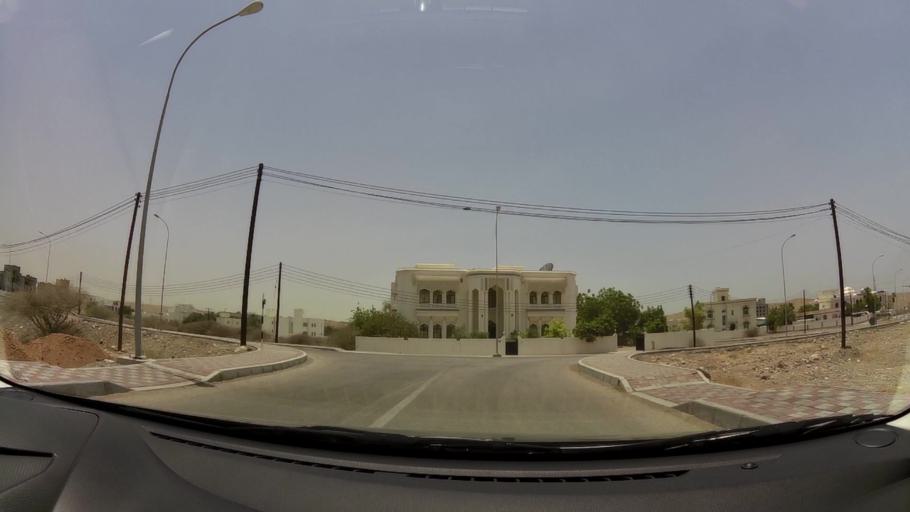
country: OM
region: Muhafazat Masqat
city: Bawshar
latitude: 23.5508
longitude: 58.4096
